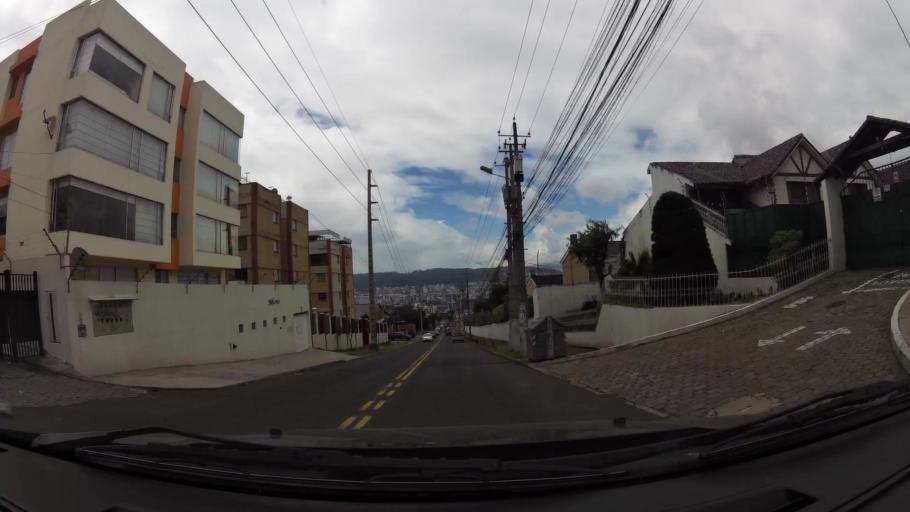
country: EC
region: Pichincha
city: Quito
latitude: -0.1756
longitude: -78.4995
